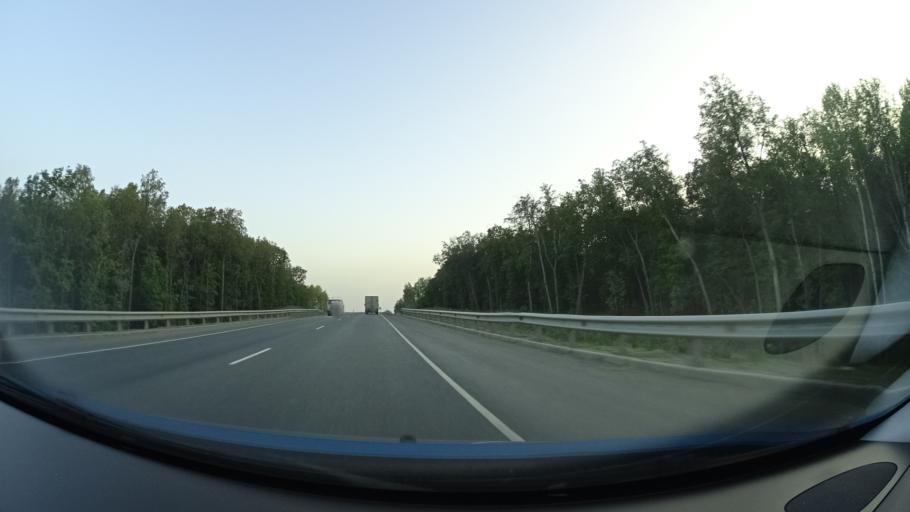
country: RU
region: Samara
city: Sernovodsk
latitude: 53.9182
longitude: 51.3066
